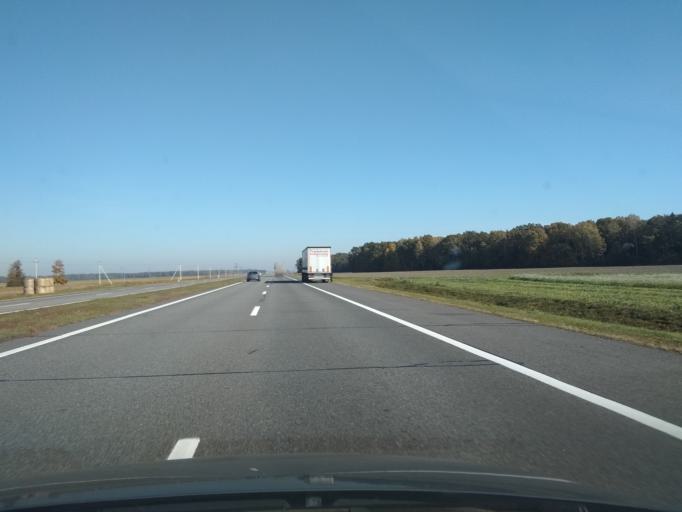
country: BY
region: Brest
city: Antopal'
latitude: 52.3948
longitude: 24.7841
